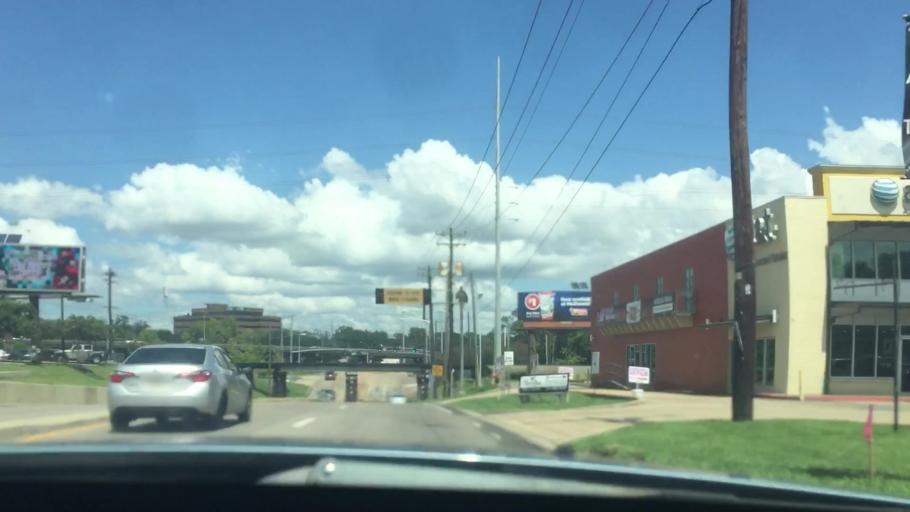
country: US
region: Louisiana
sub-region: East Baton Rouge Parish
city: Baton Rouge
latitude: 30.4213
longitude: -91.1526
